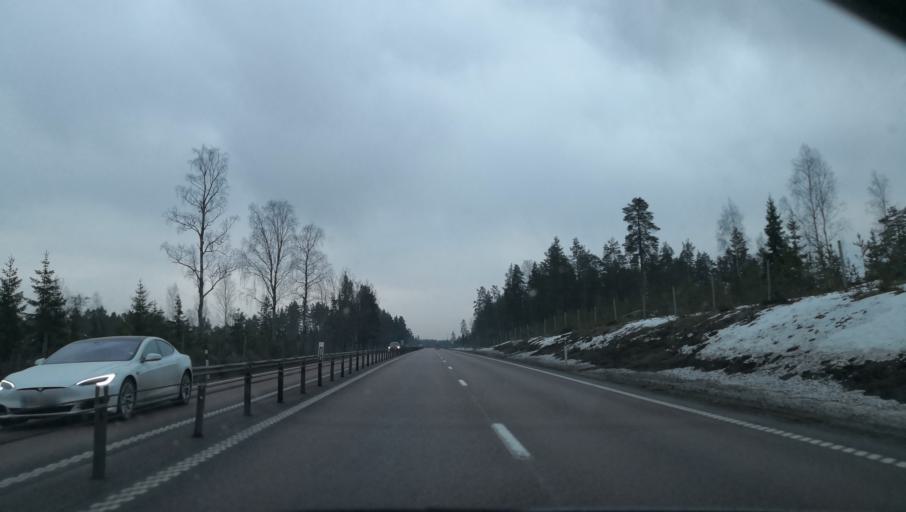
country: SE
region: Gaevleborg
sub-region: Nordanstigs Kommun
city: Bergsjoe
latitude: 61.8867
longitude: 17.1936
